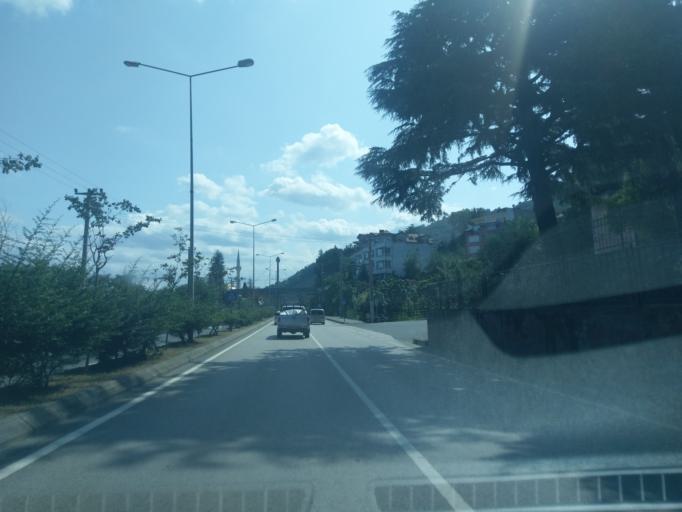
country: TR
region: Ordu
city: Ordu
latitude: 41.0056
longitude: 37.8697
